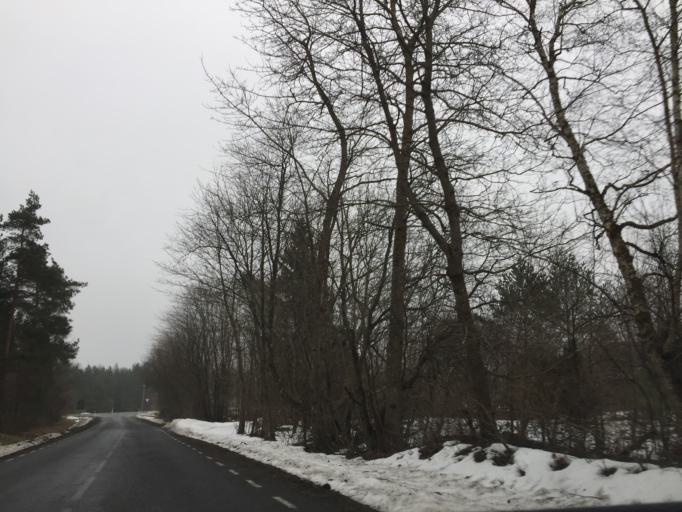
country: EE
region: Saare
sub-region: Kuressaare linn
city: Kuressaare
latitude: 58.2663
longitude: 22.5904
